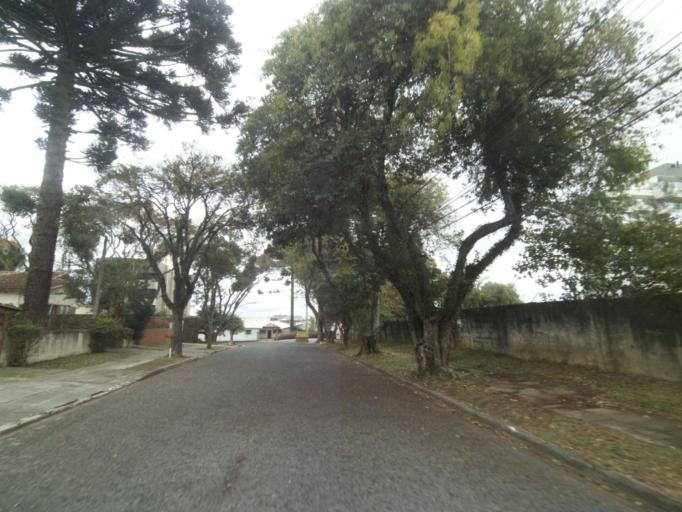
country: BR
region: Parana
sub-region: Curitiba
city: Curitiba
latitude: -25.4535
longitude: -49.2964
